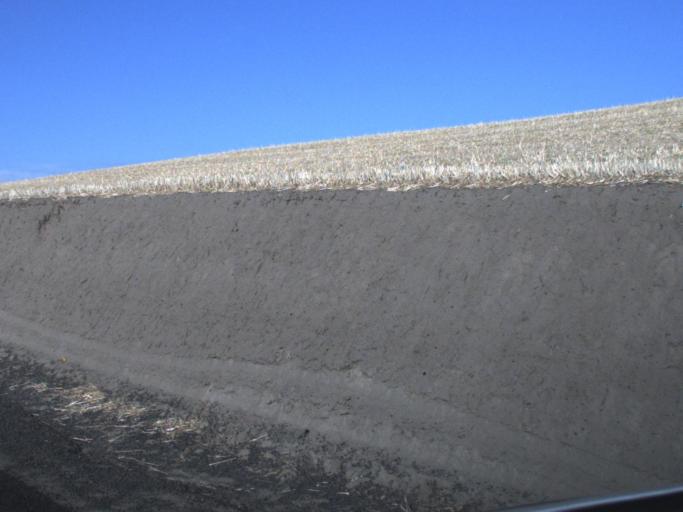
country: US
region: Washington
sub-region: Walla Walla County
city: Walla Walla
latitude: 46.1122
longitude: -118.3738
